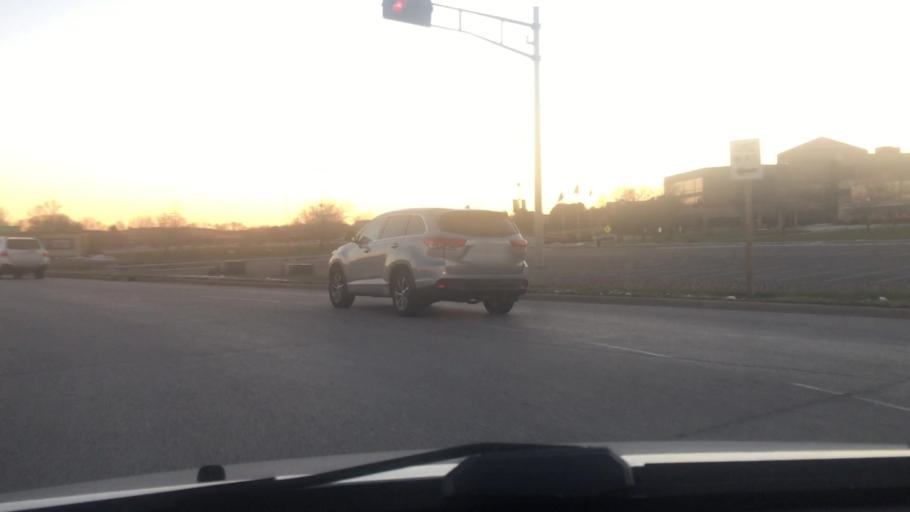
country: US
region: Wisconsin
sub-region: Waukesha County
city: Pewaukee
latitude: 43.0730
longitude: -88.2524
